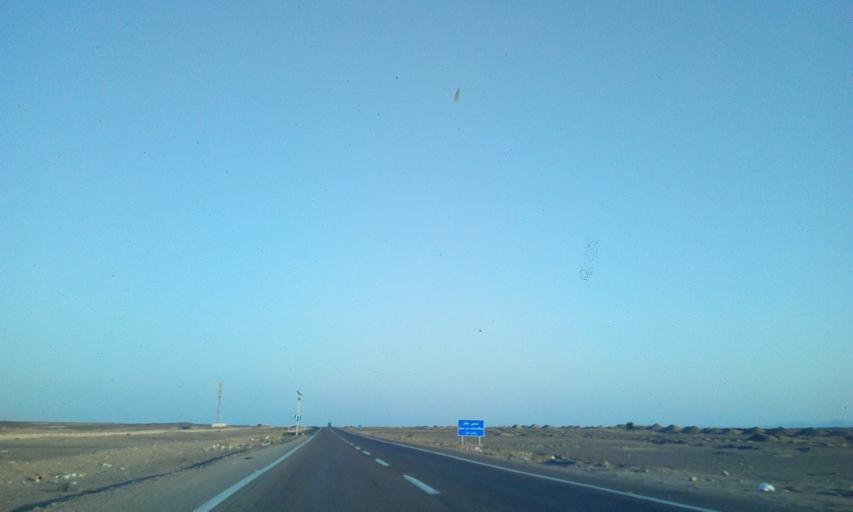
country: EG
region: South Sinai
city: Tor
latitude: 28.0254
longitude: 33.3013
